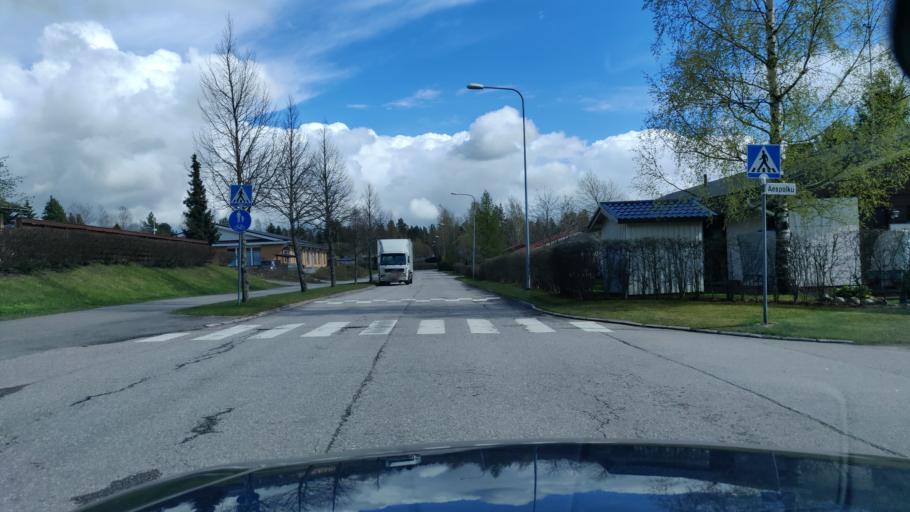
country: FI
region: Uusimaa
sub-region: Helsinki
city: Nurmijaervi
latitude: 60.3663
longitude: 24.7408
